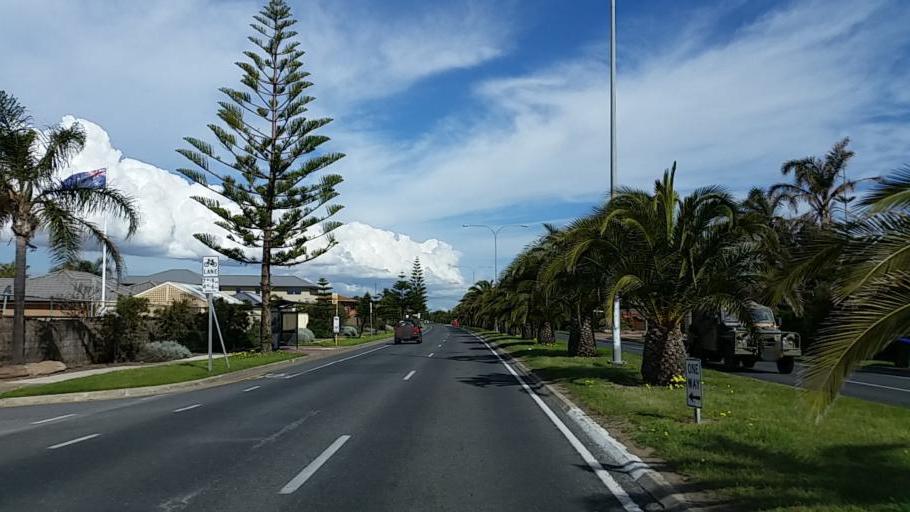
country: AU
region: South Australia
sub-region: Charles Sturt
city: West Lakes Shore
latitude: -34.8817
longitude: 138.4855
